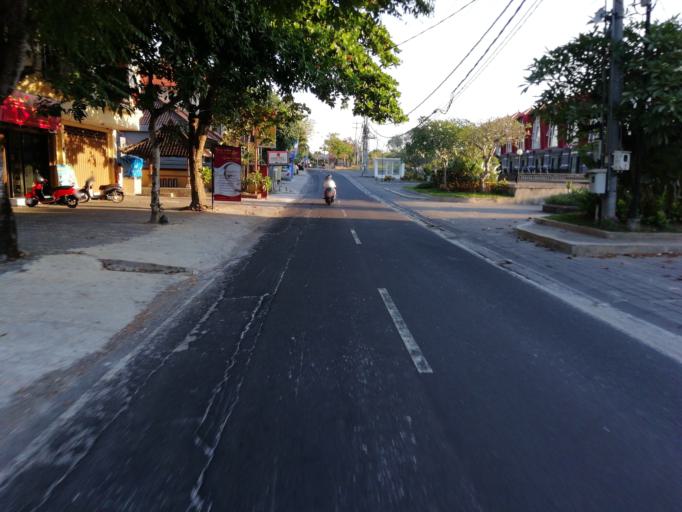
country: ID
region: Bali
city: Bualu
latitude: -8.8180
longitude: 115.1903
